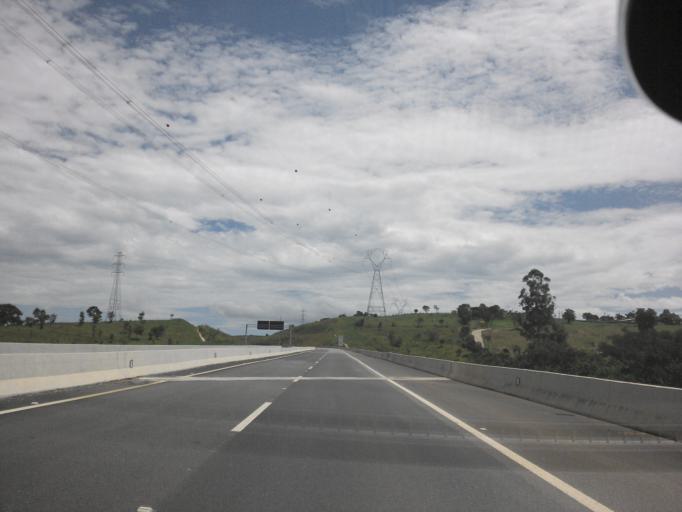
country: BR
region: Sao Paulo
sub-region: Taubate
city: Taubate
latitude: -23.0866
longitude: -45.5532
